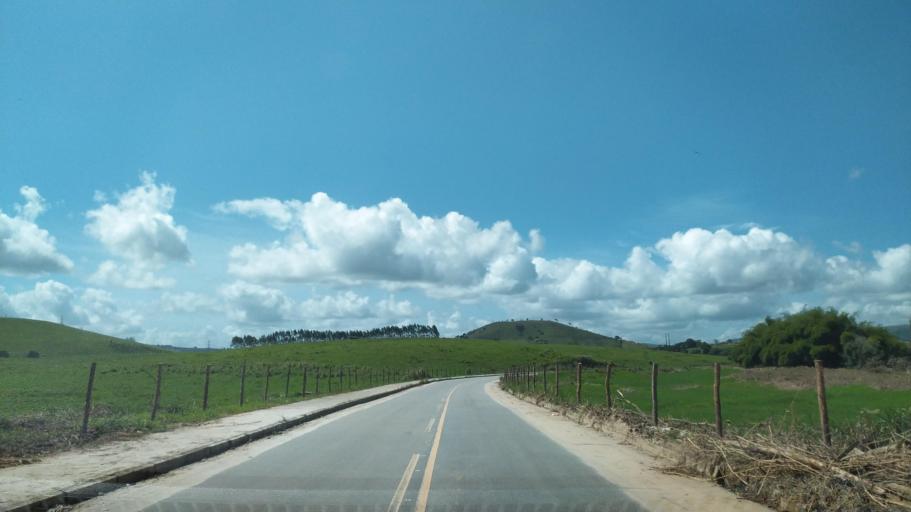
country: BR
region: Alagoas
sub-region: Uniao Dos Palmares
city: Uniao dos Palmares
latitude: -9.1582
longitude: -36.0442
